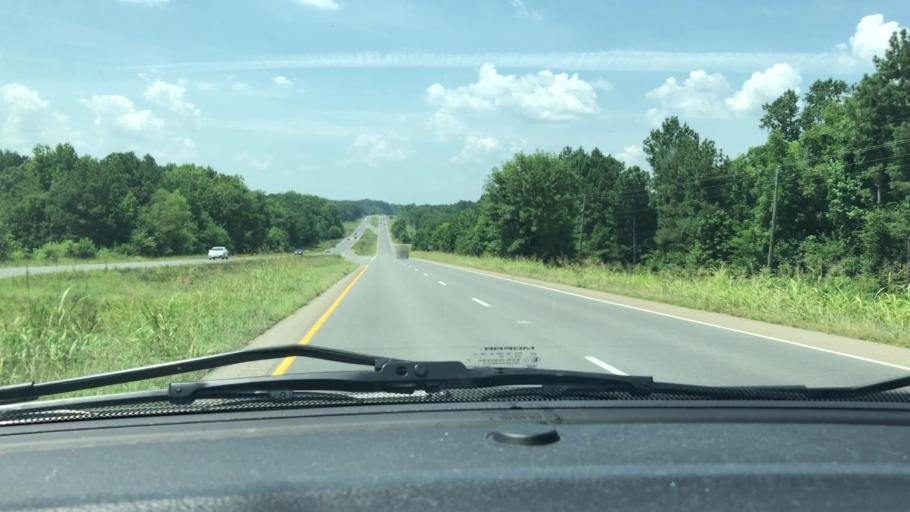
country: US
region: North Carolina
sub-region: Chatham County
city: Siler City
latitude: 35.6562
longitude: -79.3963
